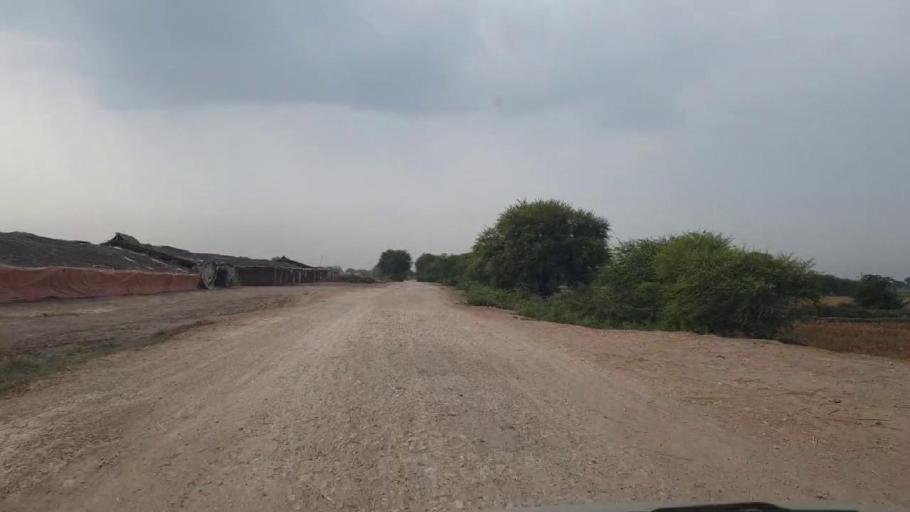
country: PK
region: Sindh
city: Talhar
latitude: 24.9180
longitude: 68.7773
